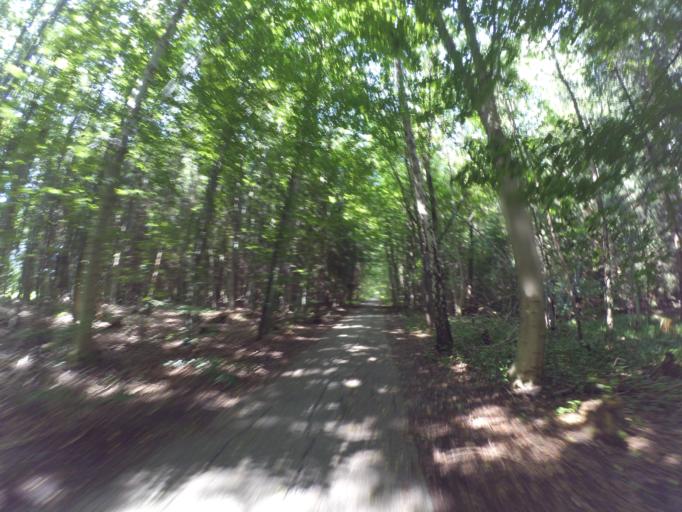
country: DE
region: Bavaria
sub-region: Swabia
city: Bad Worishofen
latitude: 48.0107
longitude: 10.5843
